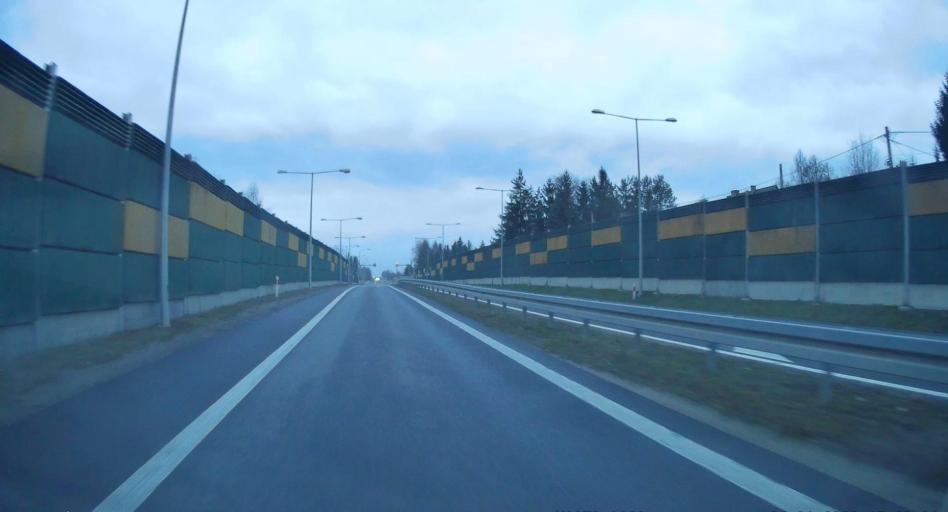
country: PL
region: Subcarpathian Voivodeship
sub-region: Powiat ropczycko-sedziszowski
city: Ropczyce
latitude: 50.0585
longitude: 21.6336
